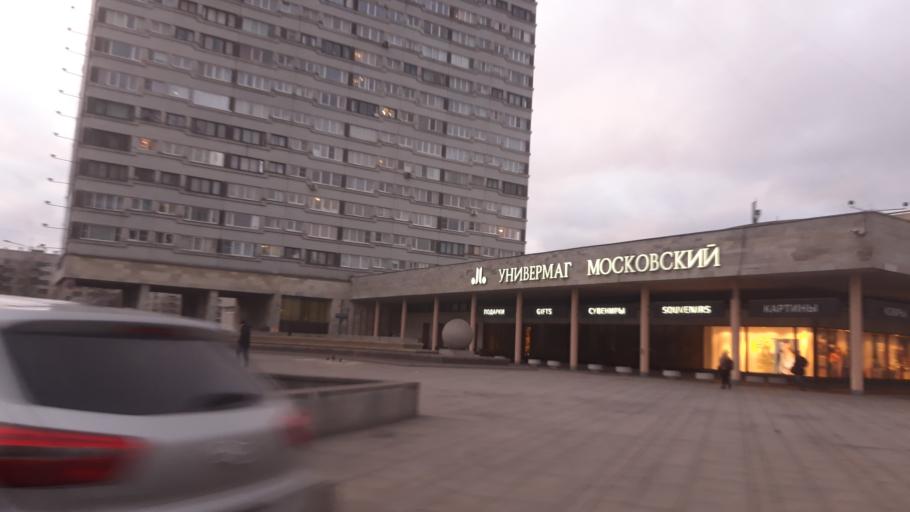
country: RU
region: St.-Petersburg
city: Kupchino
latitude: 59.8445
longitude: 30.3213
